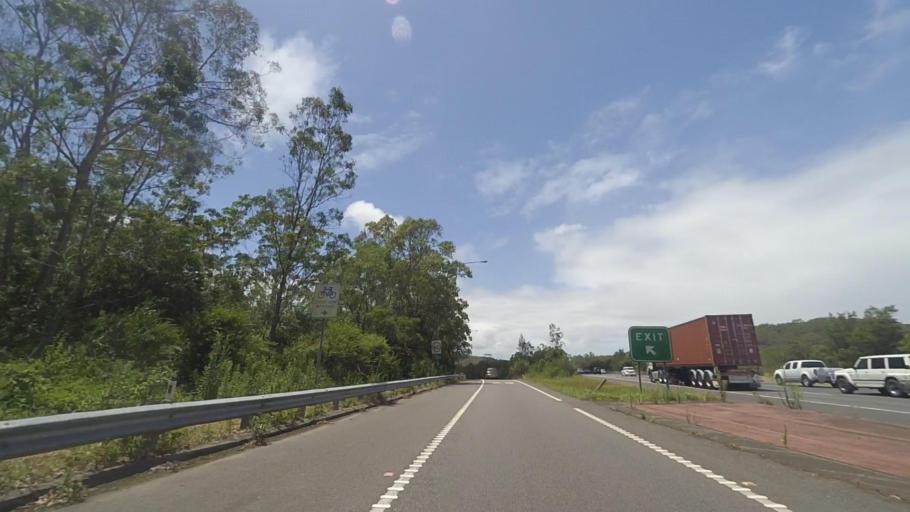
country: AU
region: New South Wales
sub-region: Gosford Shire
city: Lisarow
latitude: -33.3461
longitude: 151.3672
